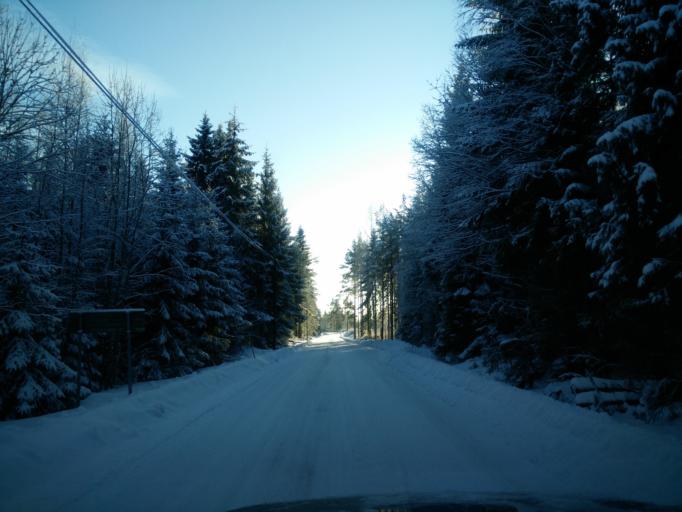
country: SE
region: Vaesternorrland
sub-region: Sundsvalls Kommun
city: Njurundabommen
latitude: 62.2125
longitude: 17.4937
